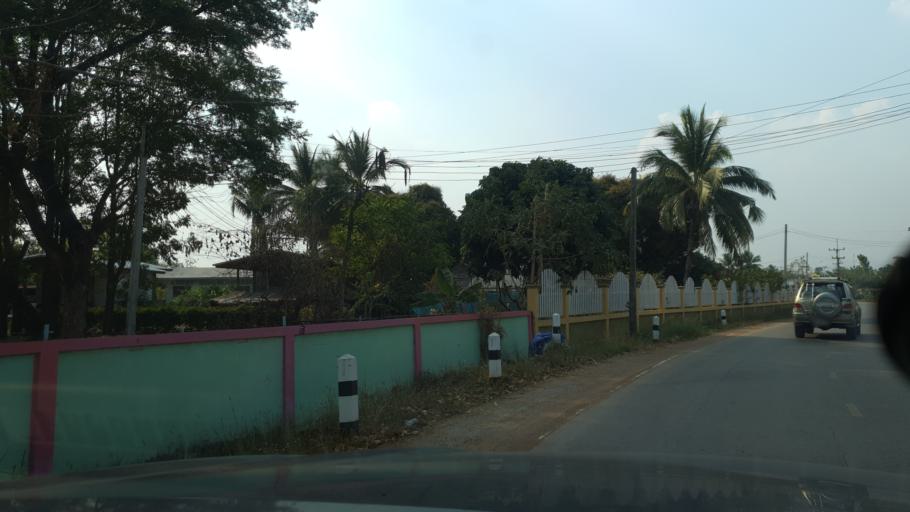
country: TH
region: Sukhothai
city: Ban Dan Lan Hoi
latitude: 17.1130
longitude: 99.5486
